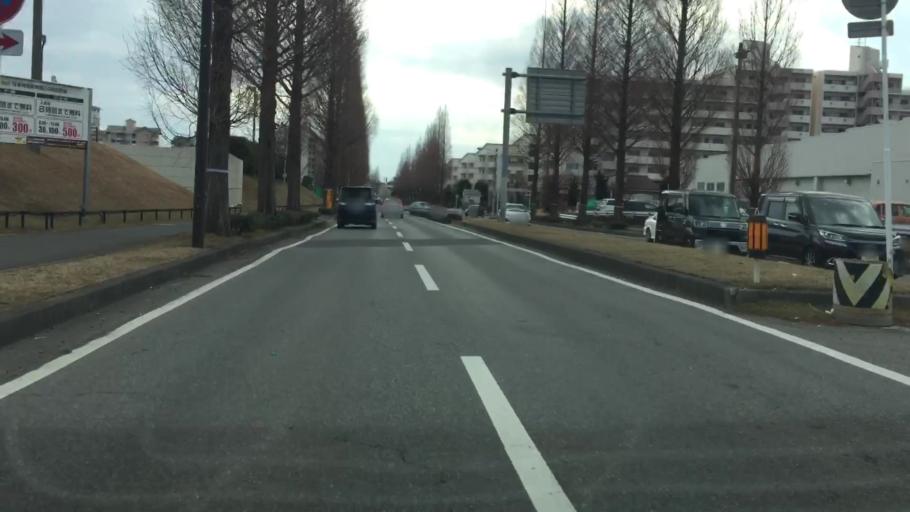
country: JP
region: Chiba
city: Shiroi
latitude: 35.8044
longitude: 140.1600
